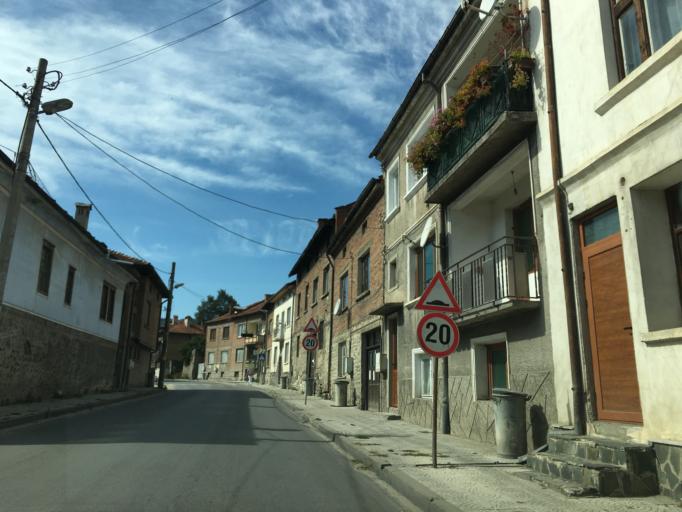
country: BG
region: Pazardzhik
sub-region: Obshtina Batak
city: Batak
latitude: 41.9441
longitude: 24.2179
